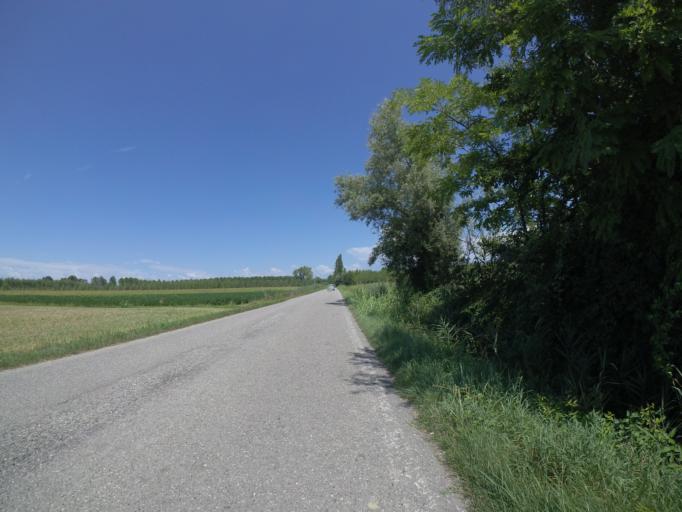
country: IT
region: Friuli Venezia Giulia
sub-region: Provincia di Udine
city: Talmassons
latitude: 45.8939
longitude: 13.1161
